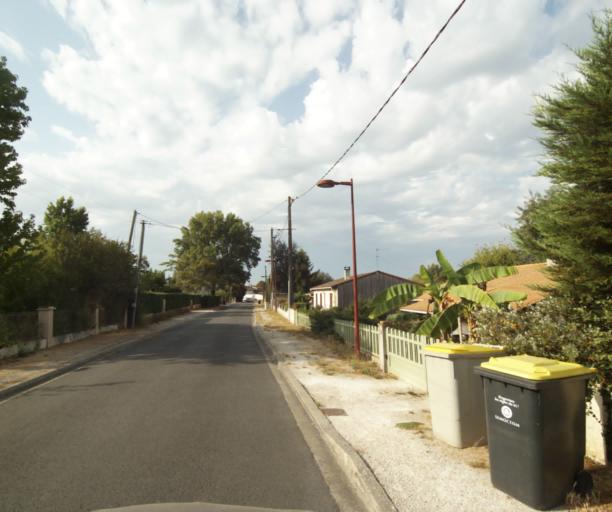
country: FR
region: Aquitaine
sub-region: Departement de la Gironde
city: Creon
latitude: 44.7645
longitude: -0.3521
